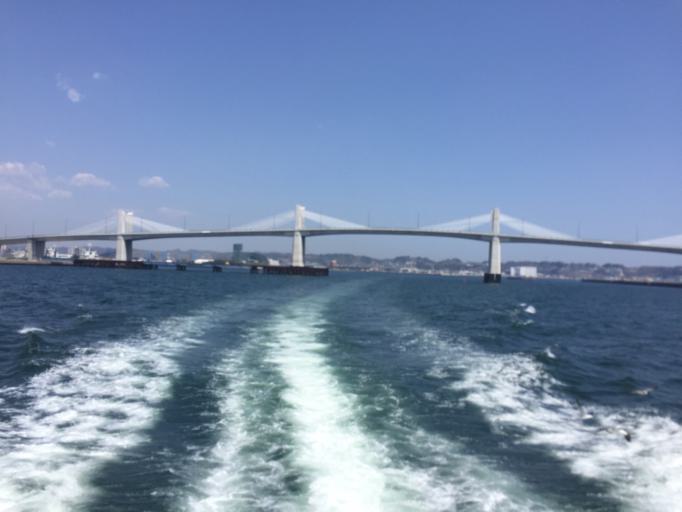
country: JP
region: Fukushima
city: Iwaki
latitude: 36.9362
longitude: 140.8948
